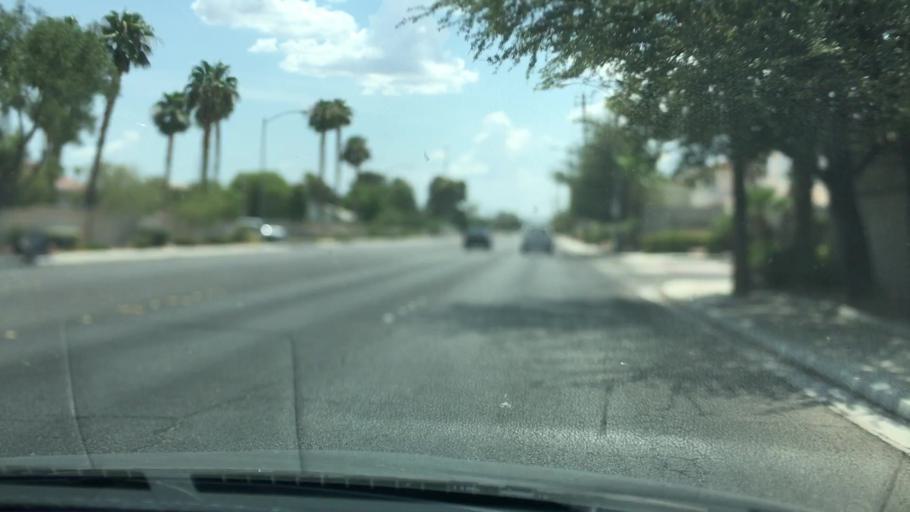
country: US
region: Nevada
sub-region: Clark County
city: Whitney
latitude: 36.0819
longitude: -115.0916
